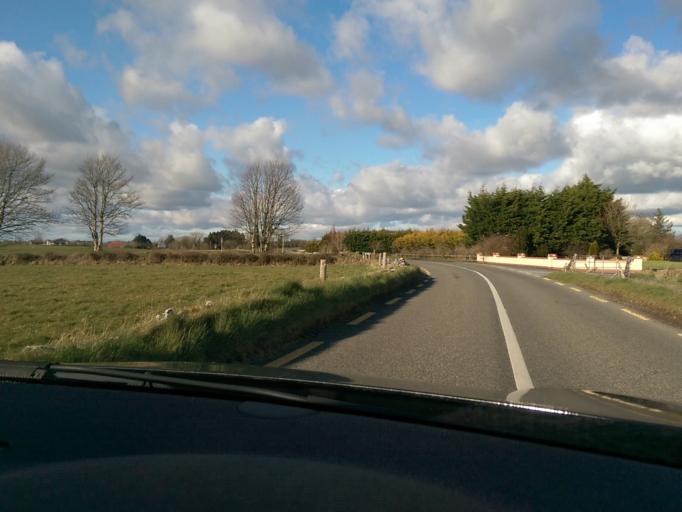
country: IE
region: Connaught
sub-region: Roscommon
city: Castlerea
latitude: 53.5761
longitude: -8.5630
